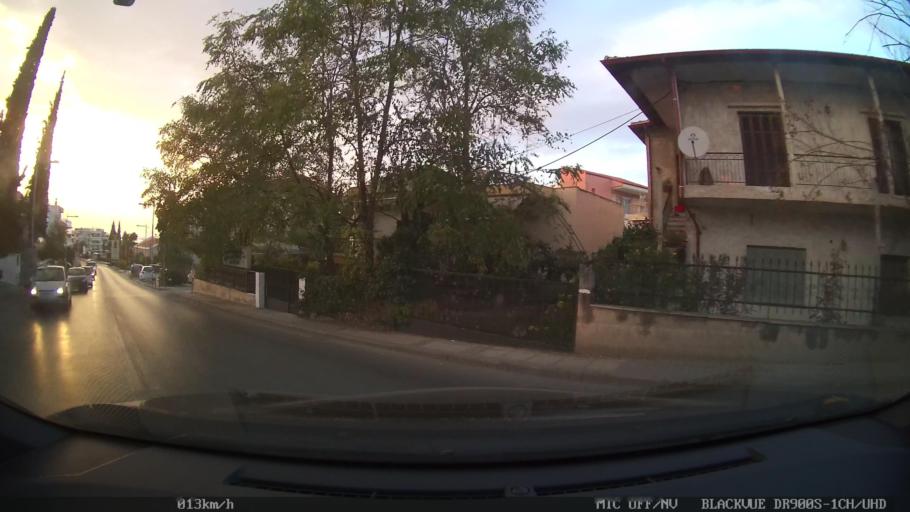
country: GR
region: Central Macedonia
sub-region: Nomos Thessalonikis
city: Pylaia
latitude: 40.6010
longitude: 22.9928
